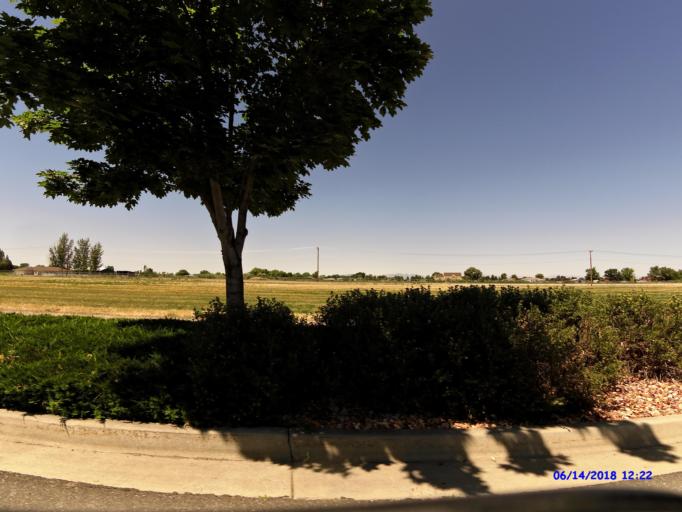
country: US
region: Utah
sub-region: Weber County
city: Marriott-Slaterville
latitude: 41.2645
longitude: -112.0076
